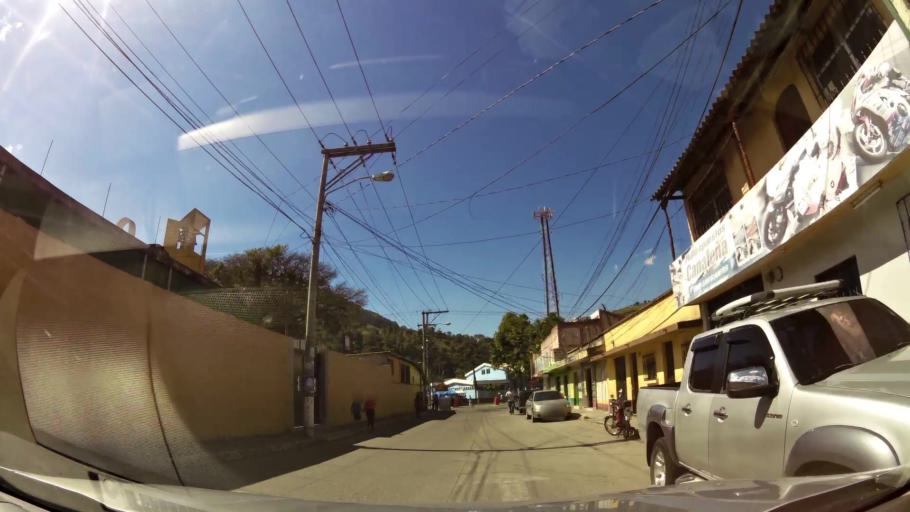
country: GT
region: Guatemala
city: Villa Canales
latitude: 14.4821
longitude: -90.5339
